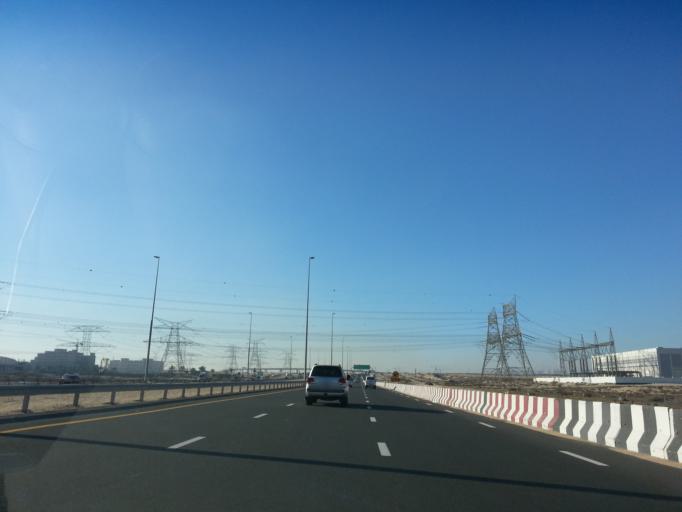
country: AE
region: Dubai
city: Dubai
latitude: 25.0074
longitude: 55.1706
